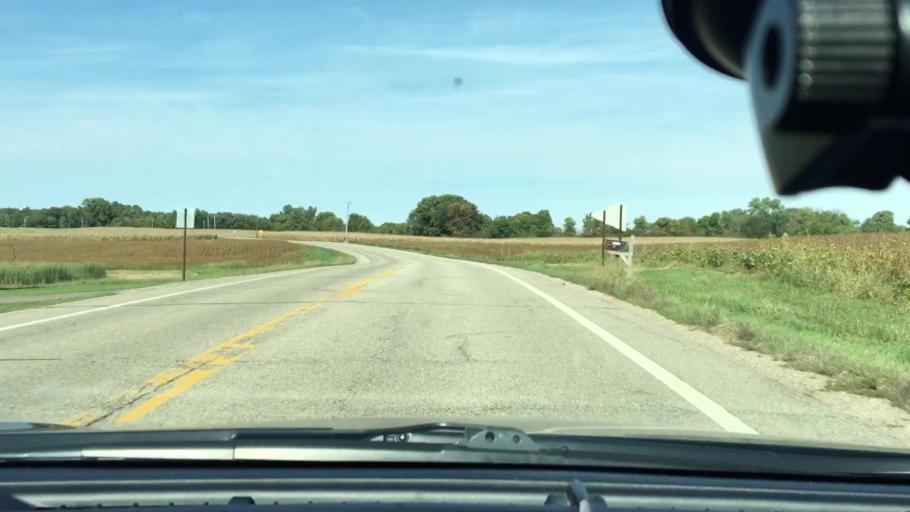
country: US
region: Minnesota
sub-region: Hennepin County
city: Corcoran
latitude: 45.1076
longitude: -93.5647
